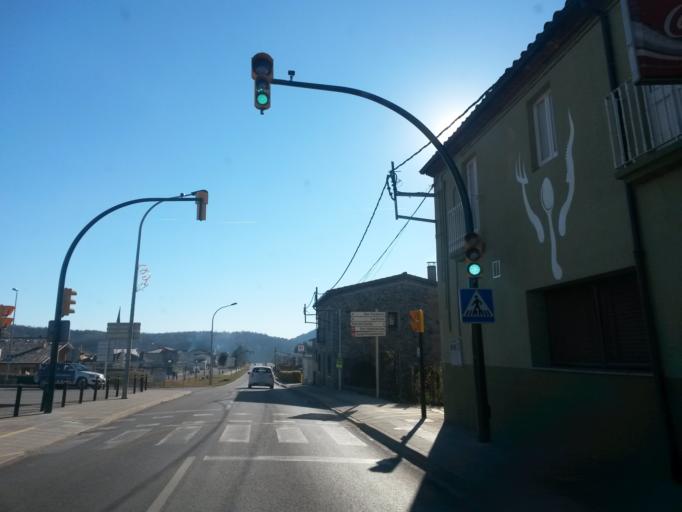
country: ES
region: Catalonia
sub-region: Provincia de Girona
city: les Planes d'Hostoles
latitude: 42.0545
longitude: 2.5433
